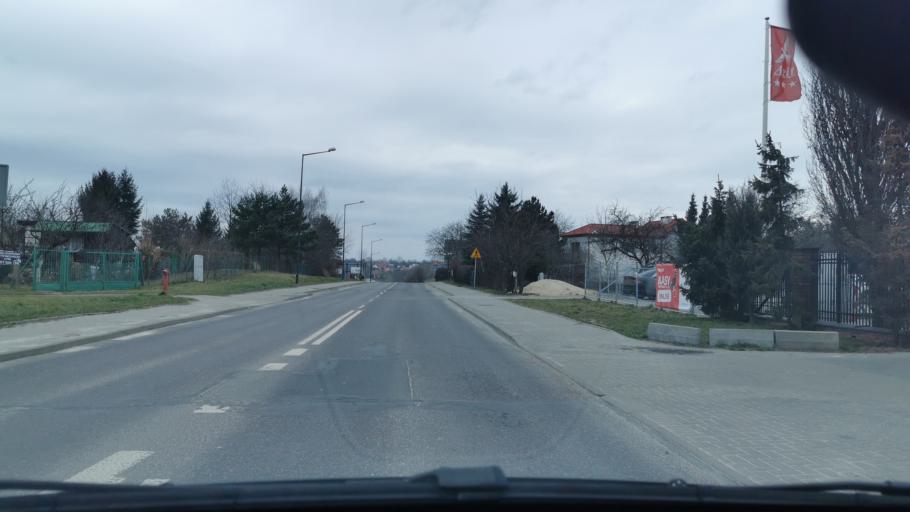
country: PL
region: Lublin Voivodeship
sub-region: Powiat lubelski
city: Lublin
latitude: 51.2472
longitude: 22.5005
